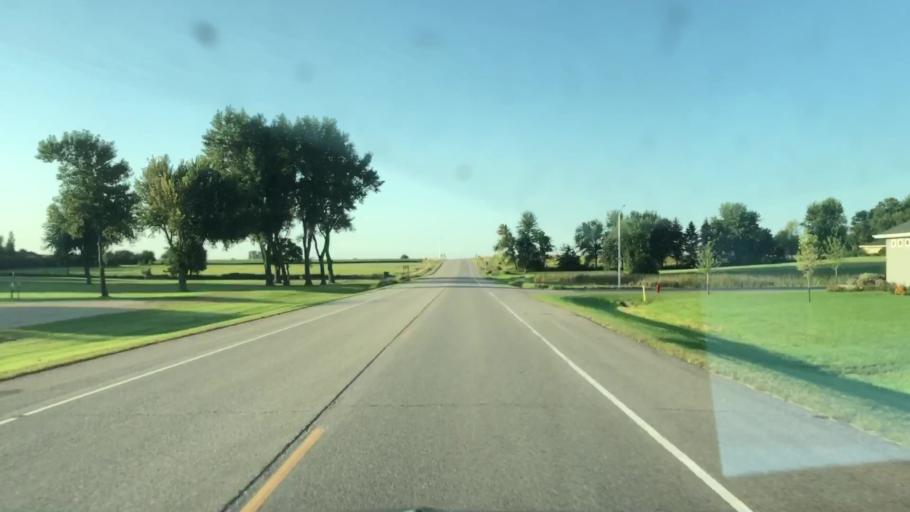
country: US
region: Minnesota
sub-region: Nobles County
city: Worthington
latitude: 43.6064
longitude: -95.6366
